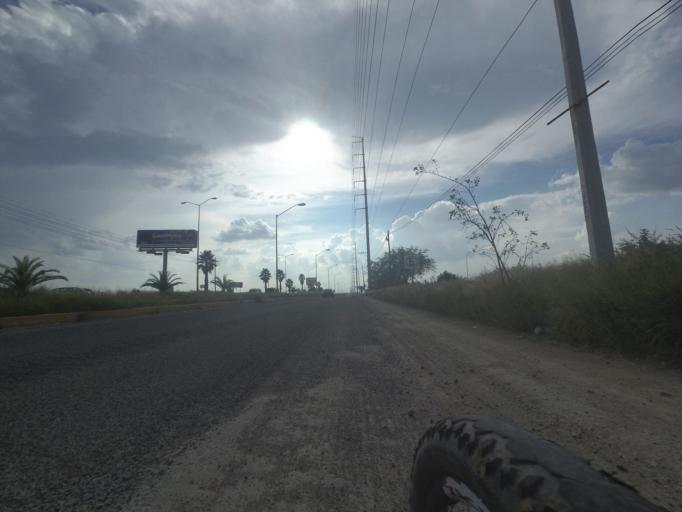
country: MX
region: Aguascalientes
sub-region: Aguascalientes
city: Penuelas (El Cienegal)
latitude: 21.7247
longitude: -102.2875
